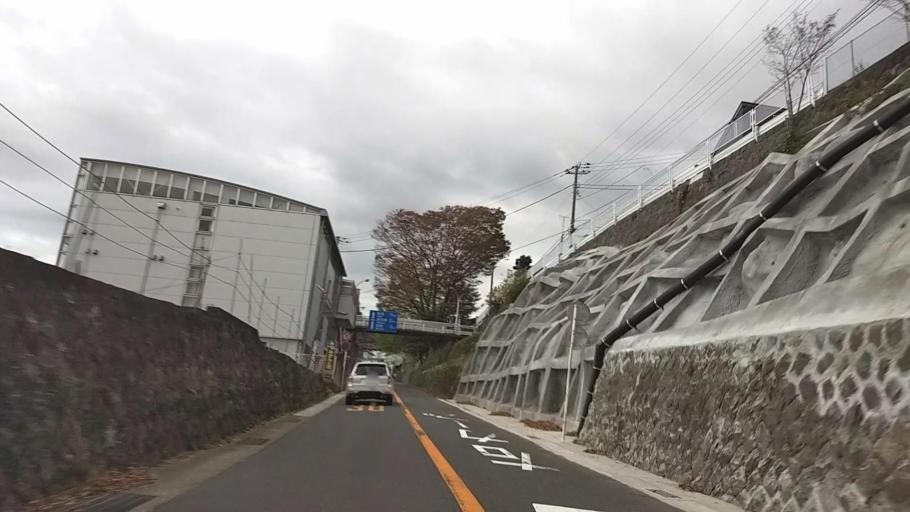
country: JP
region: Kanagawa
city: Odawara
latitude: 35.2035
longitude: 139.1386
